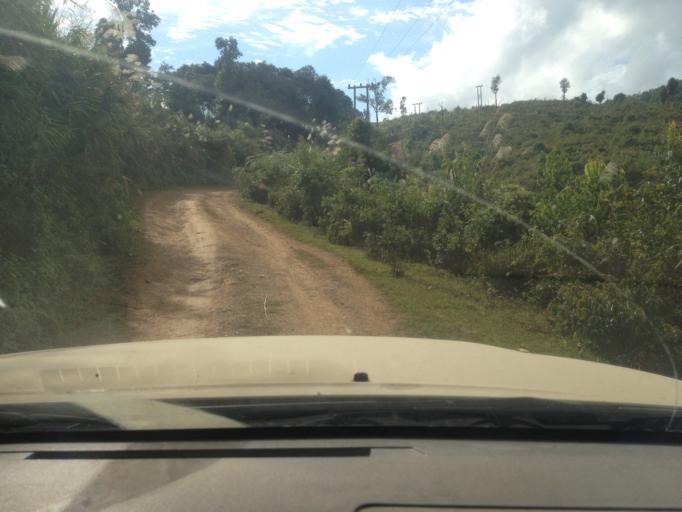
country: TH
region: Nan
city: Chaloem Phra Kiat
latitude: 19.9614
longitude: 101.0176
